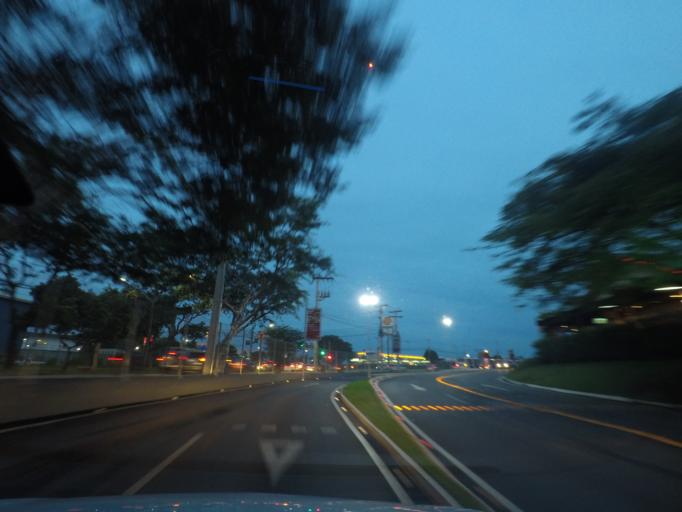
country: BR
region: Goias
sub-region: Goiania
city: Goiania
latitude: -16.7083
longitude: -49.2359
